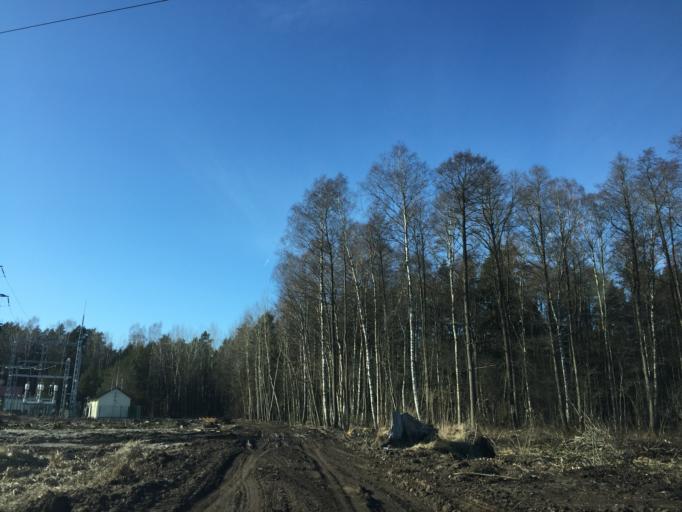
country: LV
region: Babite
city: Pinki
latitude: 56.9664
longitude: 23.8852
